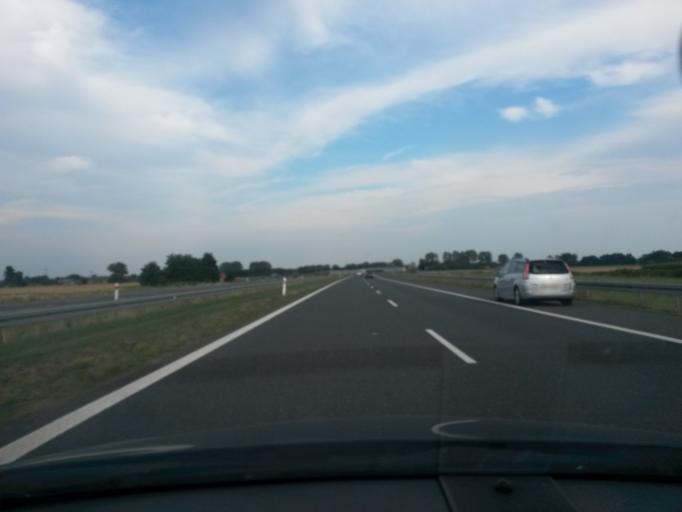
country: PL
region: Lodz Voivodeship
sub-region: Powiat leczycki
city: Swinice Warckie
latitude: 52.0127
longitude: 18.9611
